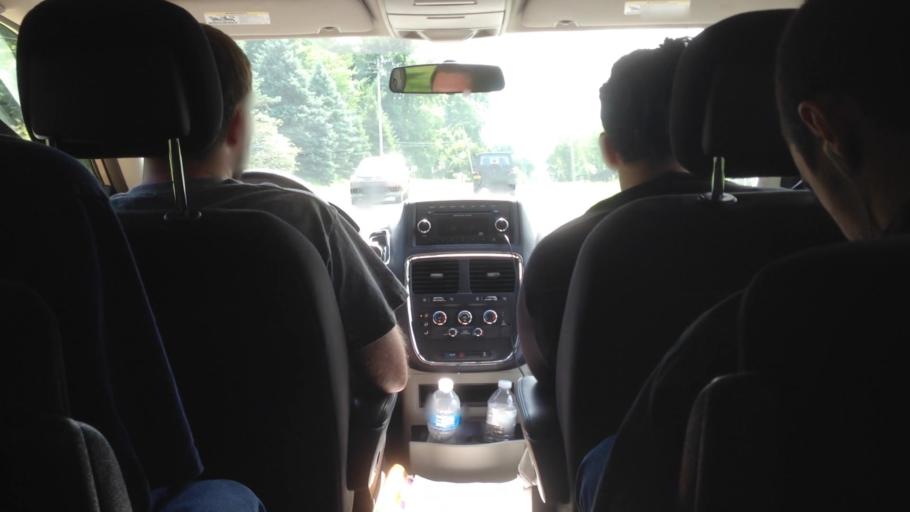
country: US
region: New York
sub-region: Dutchess County
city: Tivoli
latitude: 42.0885
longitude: -73.8955
